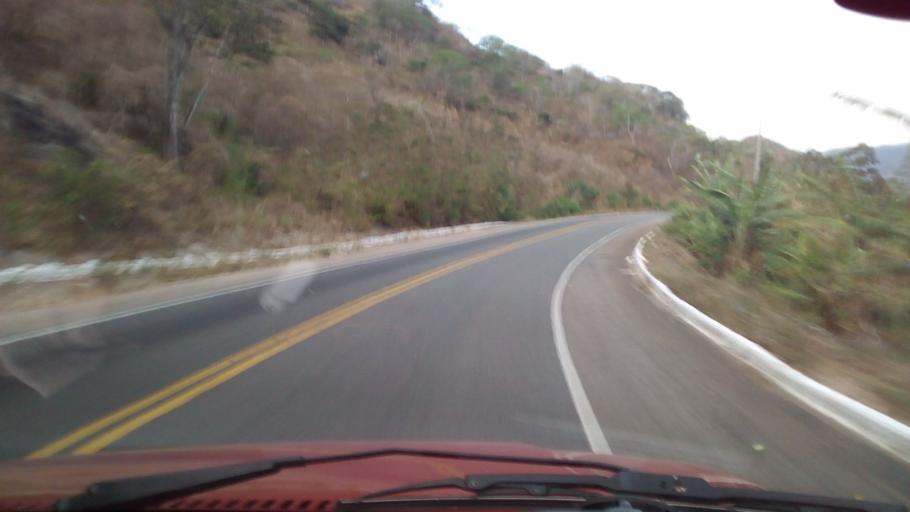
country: BR
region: Paraiba
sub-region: Bananeiras
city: Solanea
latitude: -6.7422
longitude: -35.5648
